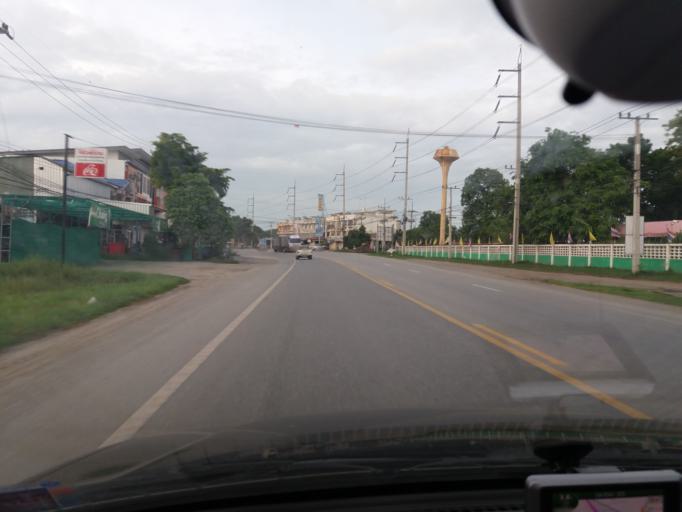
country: TH
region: Suphan Buri
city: U Thong
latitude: 14.4046
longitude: 99.8970
